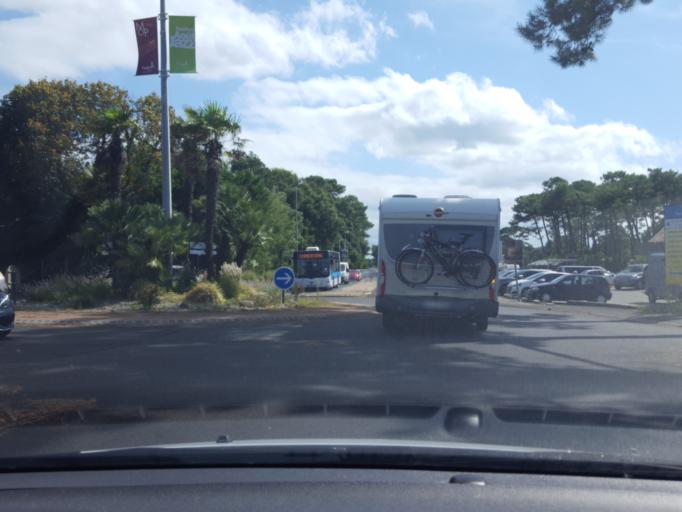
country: FR
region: Aquitaine
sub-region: Departement des Landes
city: Capbreton
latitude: 43.6392
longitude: -1.4258
